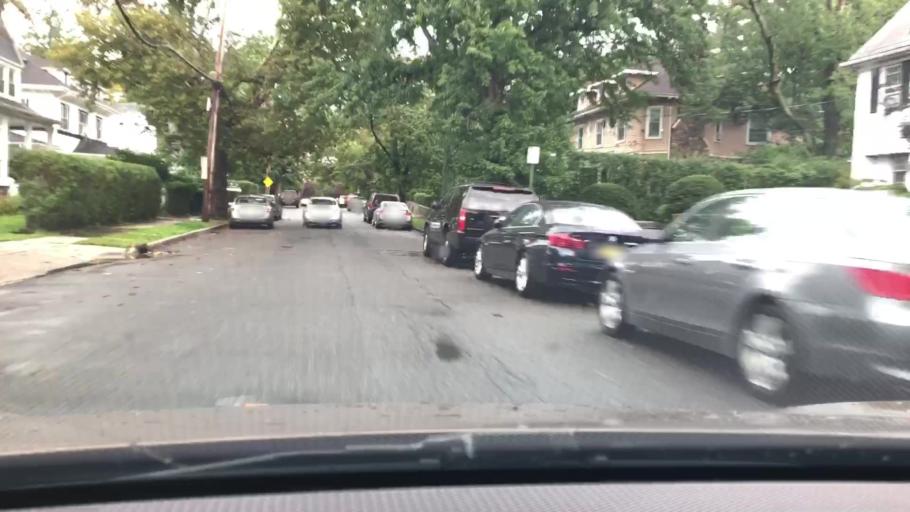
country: US
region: New York
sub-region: Westchester County
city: Mount Vernon
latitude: 40.9200
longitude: -73.8234
